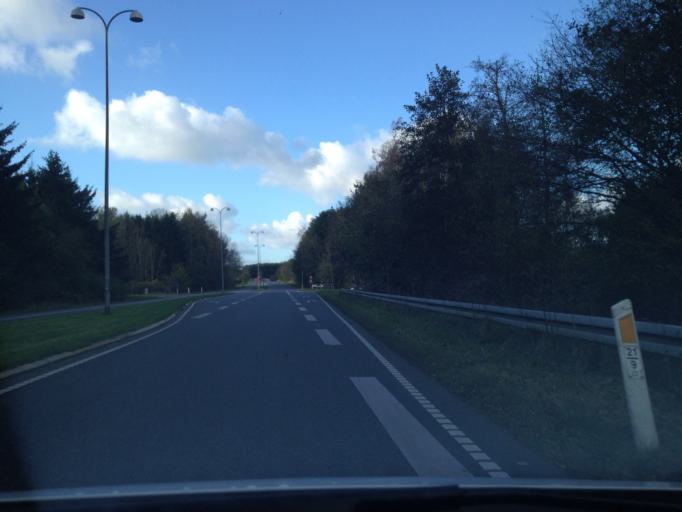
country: DK
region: Capital Region
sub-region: Fureso Kommune
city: Farum
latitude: 55.8256
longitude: 12.3708
